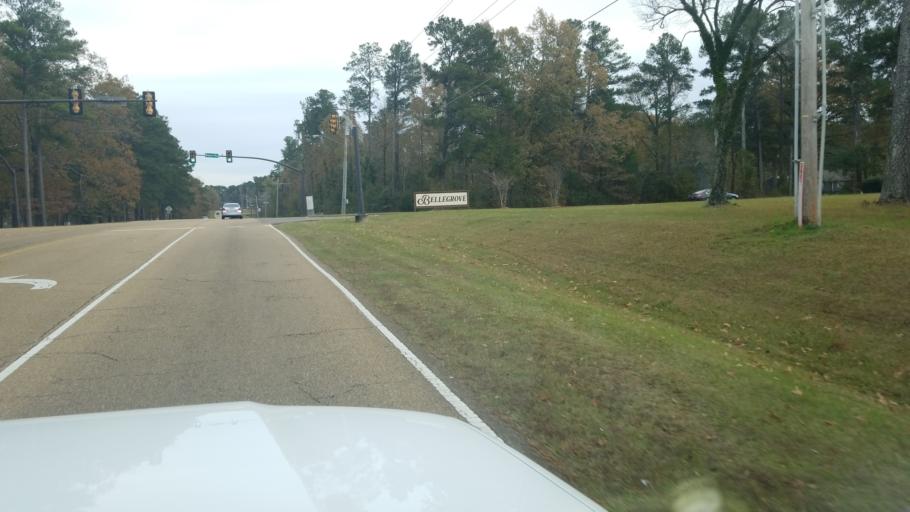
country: US
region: Mississippi
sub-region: Rankin County
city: Brandon
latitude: 32.3752
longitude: -90.0236
